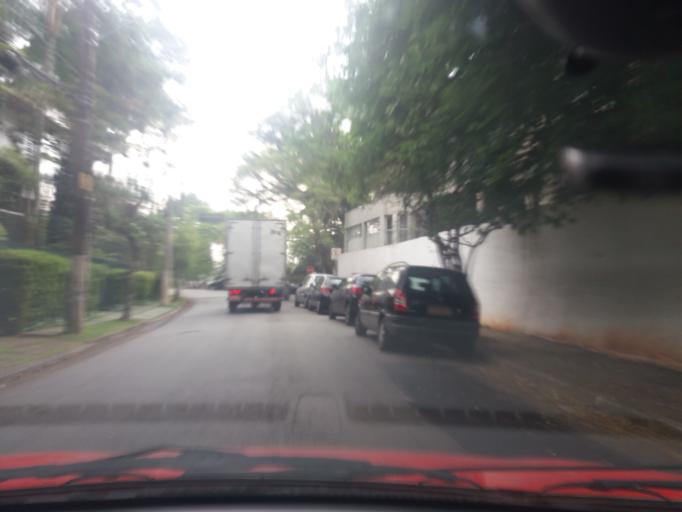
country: BR
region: Sao Paulo
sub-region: Taboao Da Serra
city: Taboao da Serra
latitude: -23.5923
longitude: -46.7115
